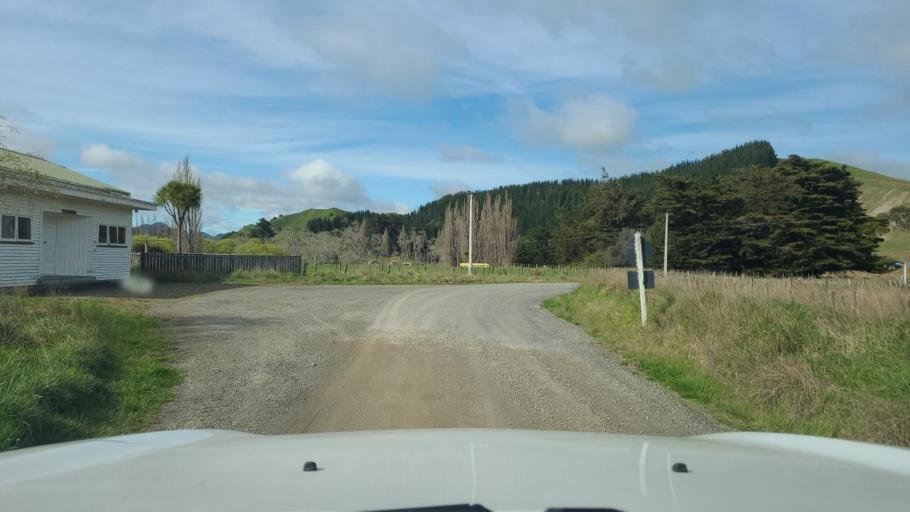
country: NZ
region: Wellington
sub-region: South Wairarapa District
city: Waipawa
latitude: -41.2941
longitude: 175.6471
